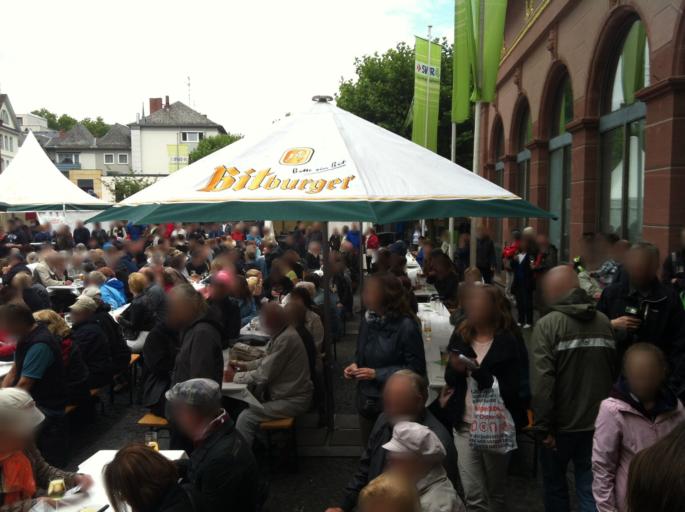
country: DE
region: Rheinland-Pfalz
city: Mainz
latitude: 49.9991
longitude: 8.2749
